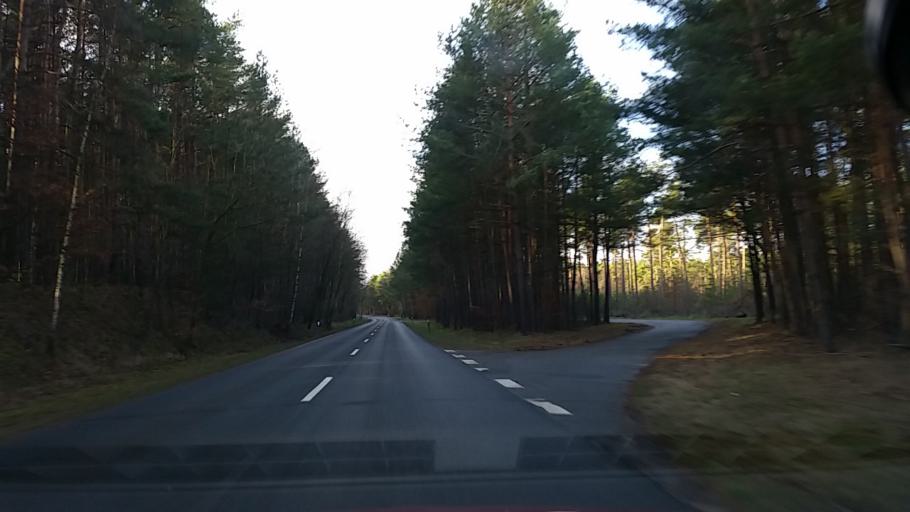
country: DE
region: Lower Saxony
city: Wieren
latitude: 52.8832
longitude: 10.6245
